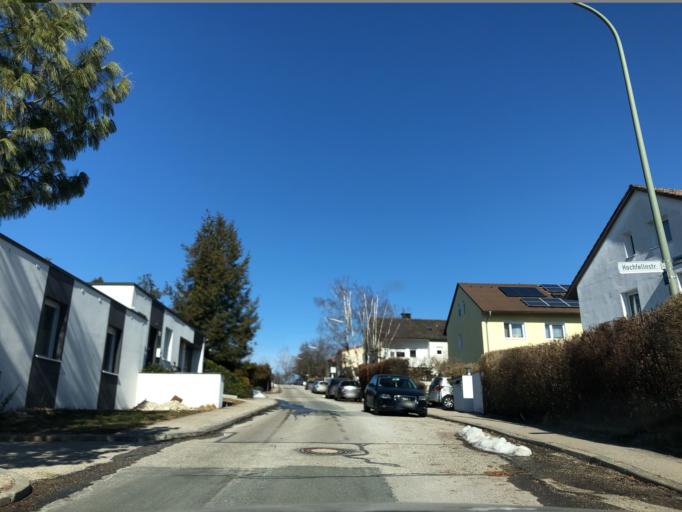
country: DE
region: Bavaria
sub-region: Upper Bavaria
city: Ebersberg
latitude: 48.0708
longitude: 11.9640
